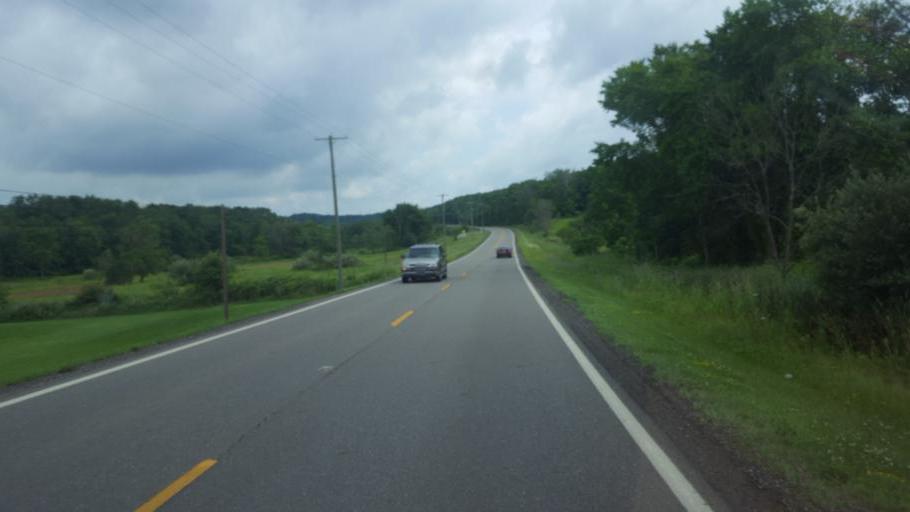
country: US
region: Ohio
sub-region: Columbiana County
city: Lisbon
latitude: 40.7340
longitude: -80.7897
